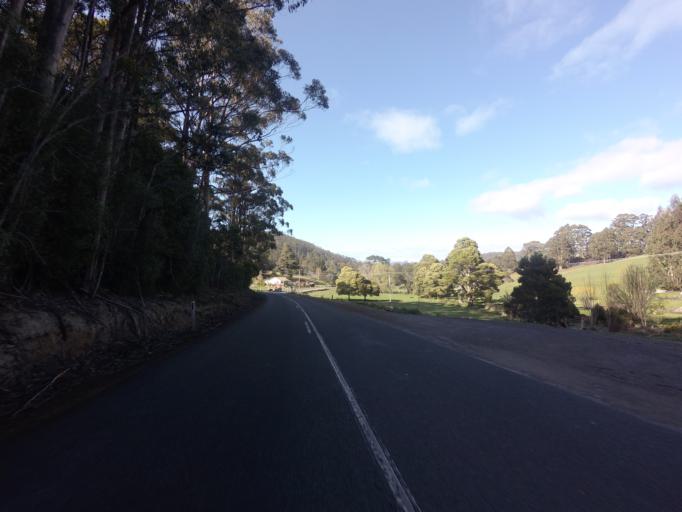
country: AU
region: Tasmania
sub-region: Huon Valley
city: Cygnet
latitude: -43.2665
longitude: 147.0108
